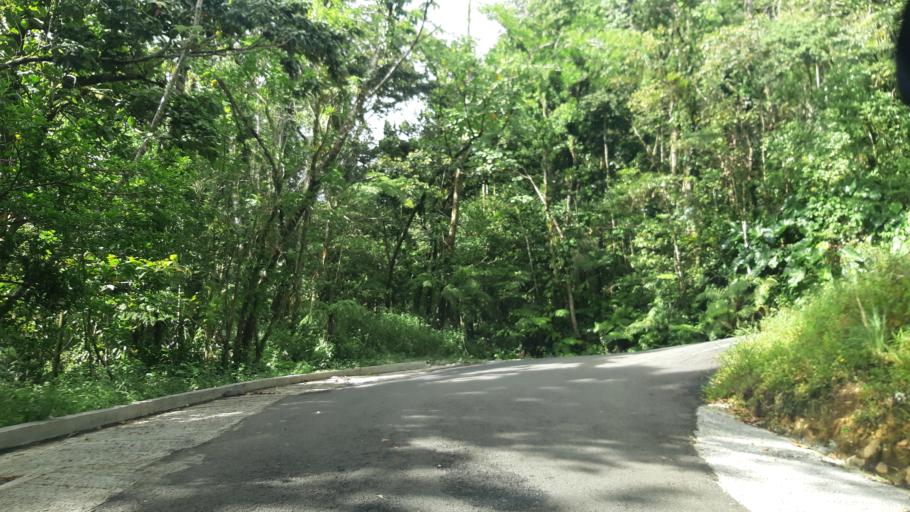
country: GP
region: Guadeloupe
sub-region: Guadeloupe
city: Saint-Claude
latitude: 16.0336
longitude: -61.6755
